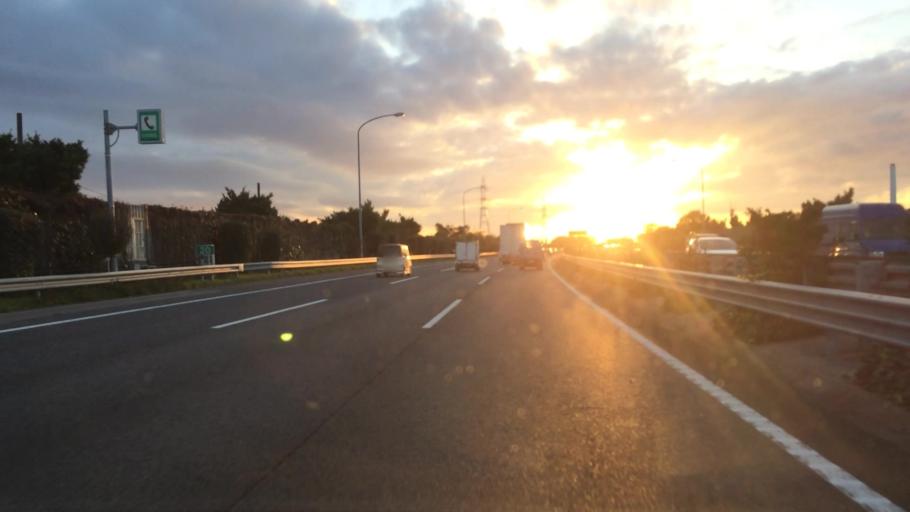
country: JP
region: Chiba
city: Yotsukaido
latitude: 35.6747
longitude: 140.1310
